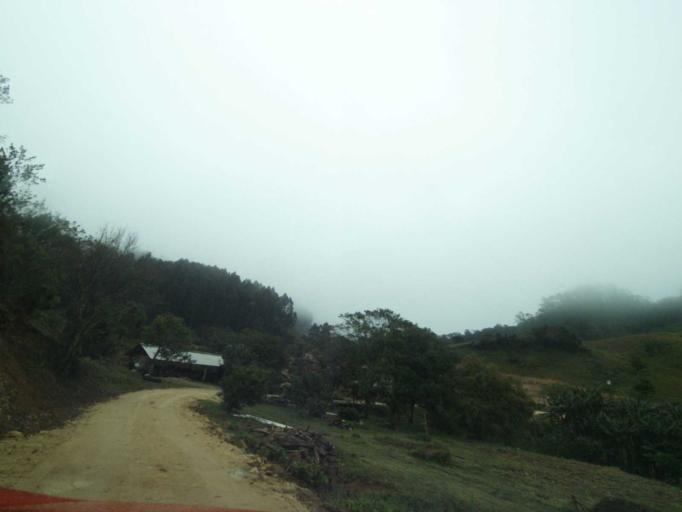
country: BR
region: Santa Catarina
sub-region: Anitapolis
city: Anitapolis
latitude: -27.9198
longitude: -49.1987
